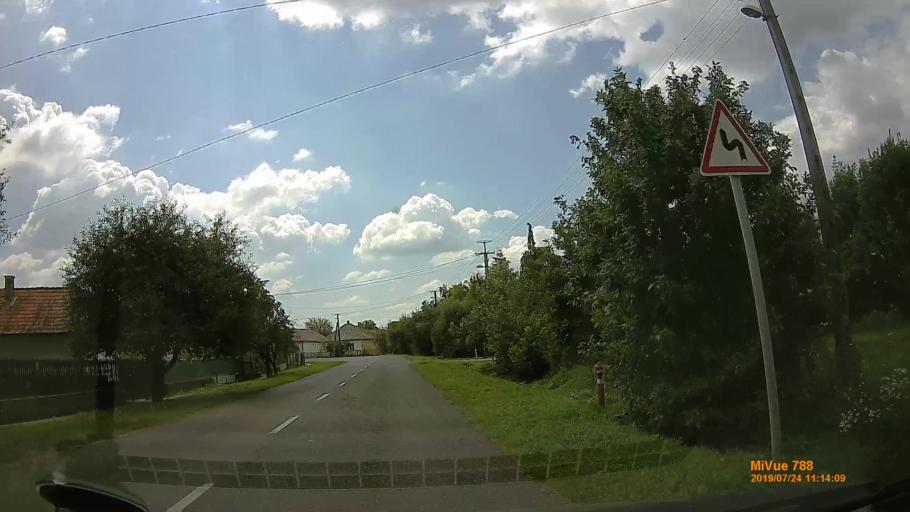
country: HU
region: Szabolcs-Szatmar-Bereg
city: Tarpa
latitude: 48.1975
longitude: 22.4469
